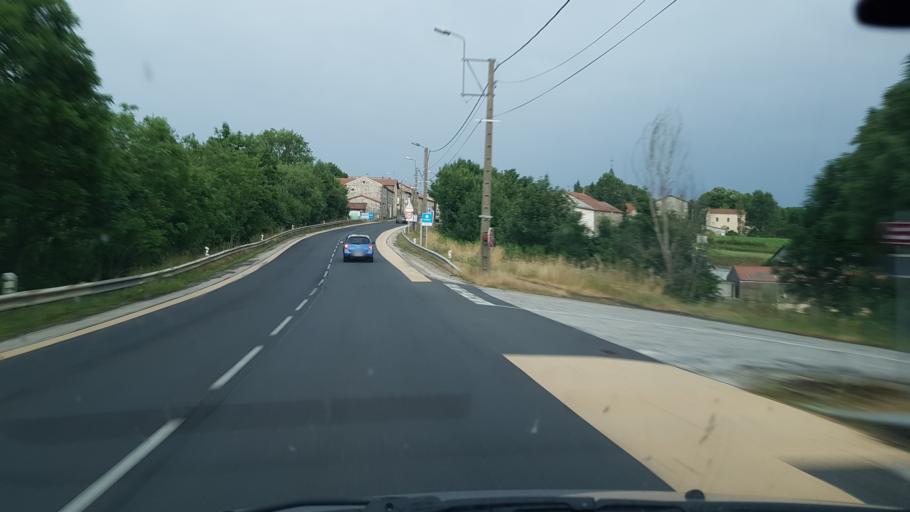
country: FR
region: Auvergne
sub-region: Departement de la Haute-Loire
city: Allegre
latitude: 45.1457
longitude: 3.6654
